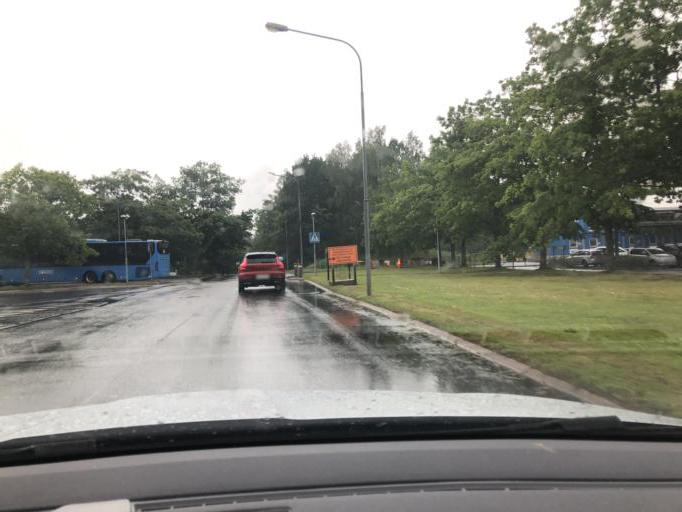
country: SE
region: Vaestra Goetaland
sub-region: Skovde Kommun
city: Skoevde
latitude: 58.4268
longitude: 13.8545
